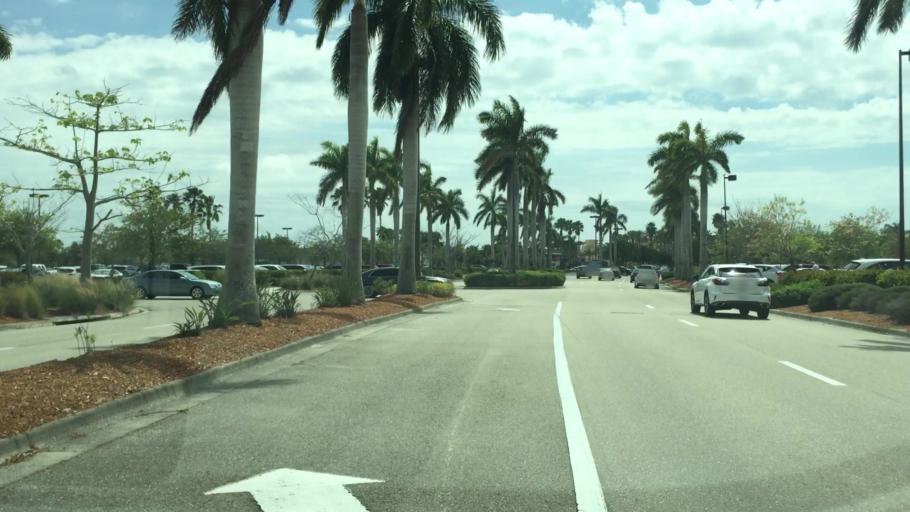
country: US
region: Florida
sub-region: Lee County
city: Three Oaks
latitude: 26.4900
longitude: -81.7873
